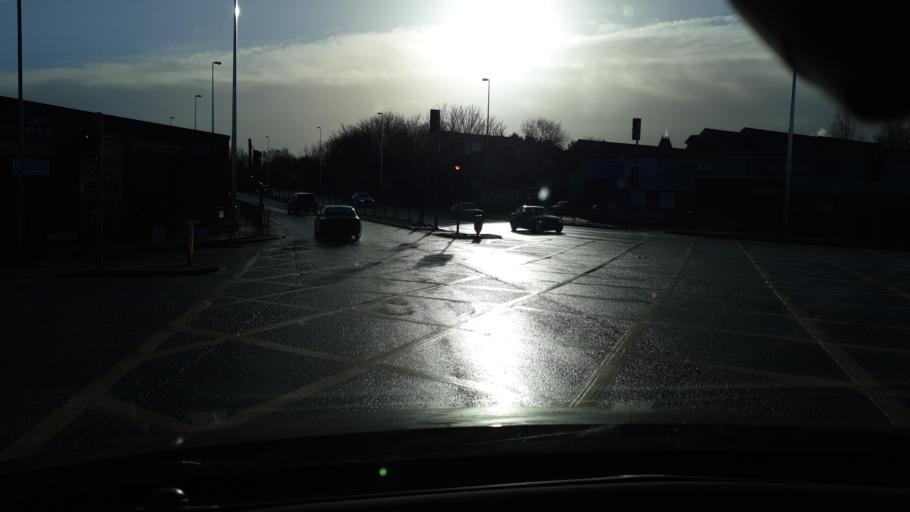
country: GB
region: England
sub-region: City and Borough of Birmingham
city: Birmingham
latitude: 52.5076
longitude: -1.8645
